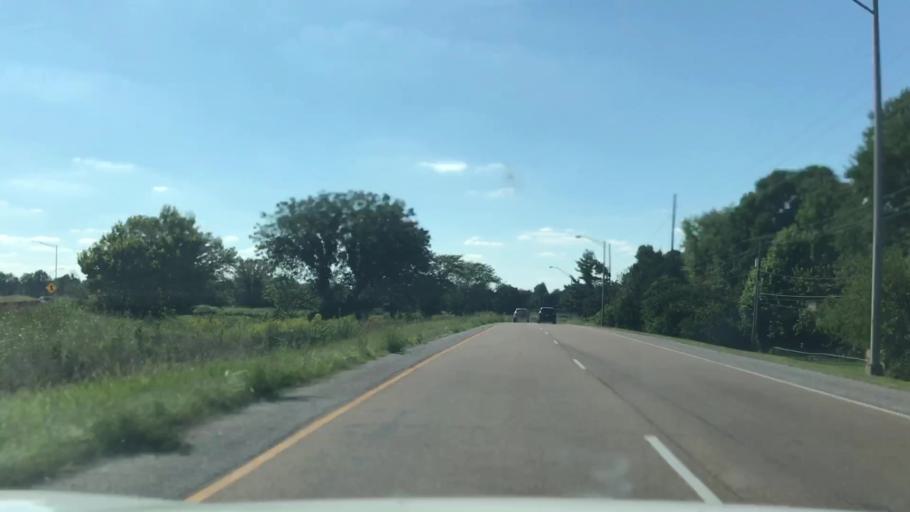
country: US
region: Illinois
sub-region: Saint Clair County
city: Swansea
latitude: 38.5478
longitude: -90.0605
